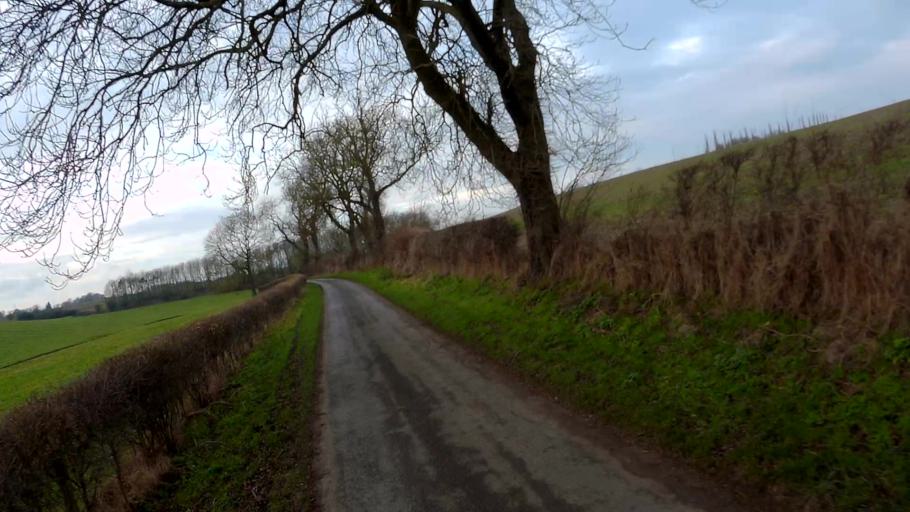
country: GB
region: England
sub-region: Lincolnshire
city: Bourne
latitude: 52.8286
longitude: -0.4675
